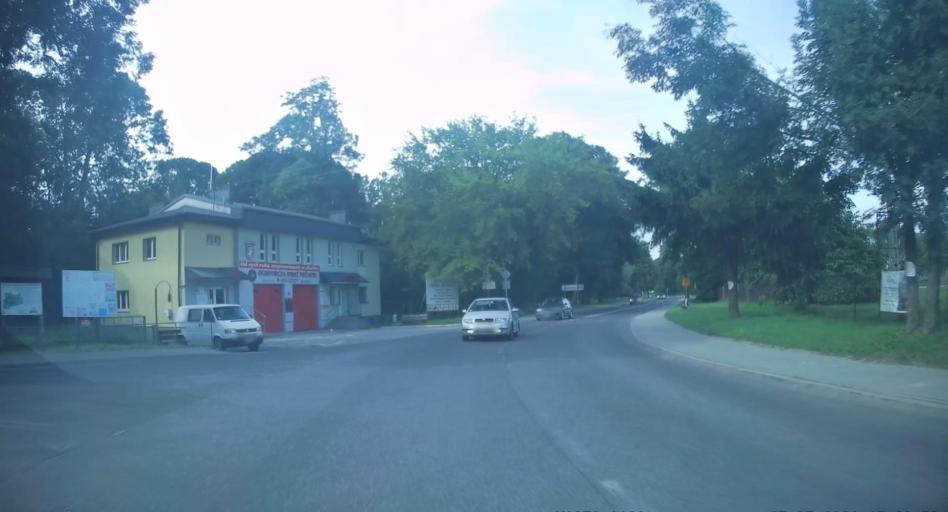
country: PL
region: Lodz Voivodeship
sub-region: Powiat tomaszowski
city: Rzeczyca
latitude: 51.5966
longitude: 20.2921
